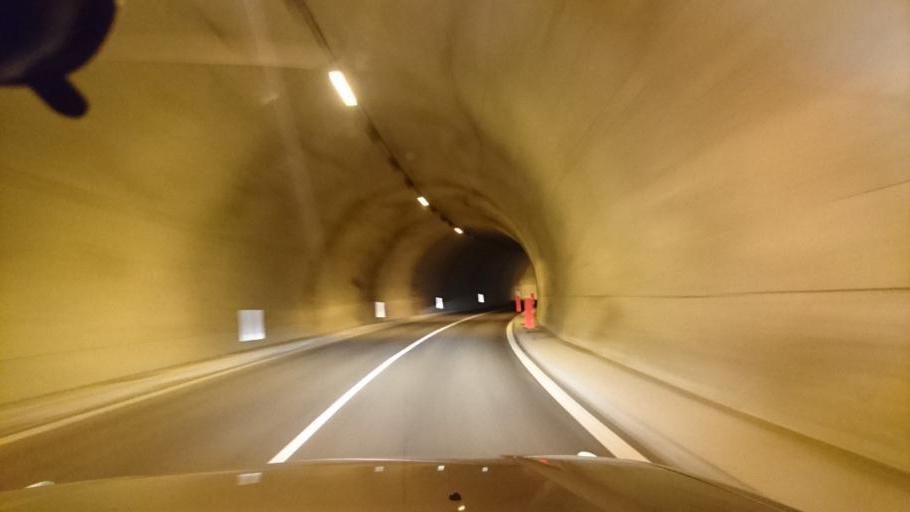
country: IT
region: Aosta Valley
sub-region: Valle d'Aosta
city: Avise
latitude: 45.7084
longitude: 7.1366
